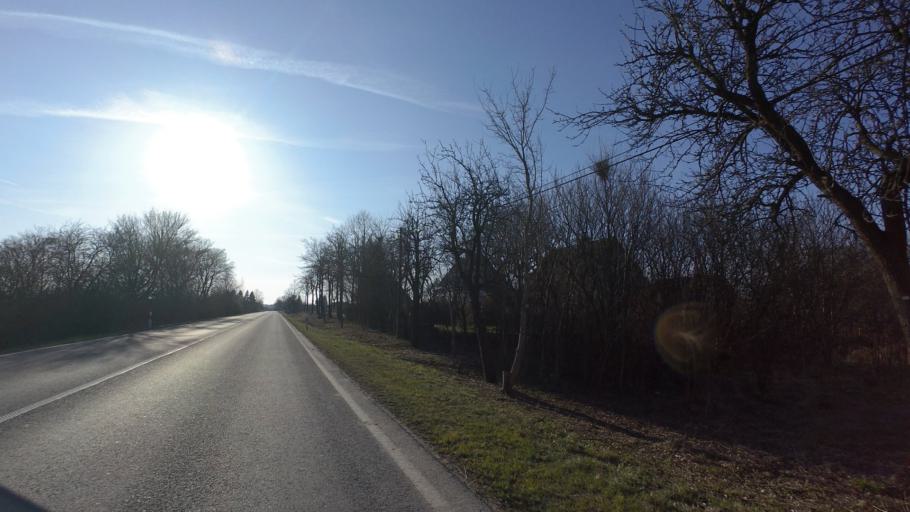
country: DE
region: Brandenburg
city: Chorin
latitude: 52.9551
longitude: 13.8962
